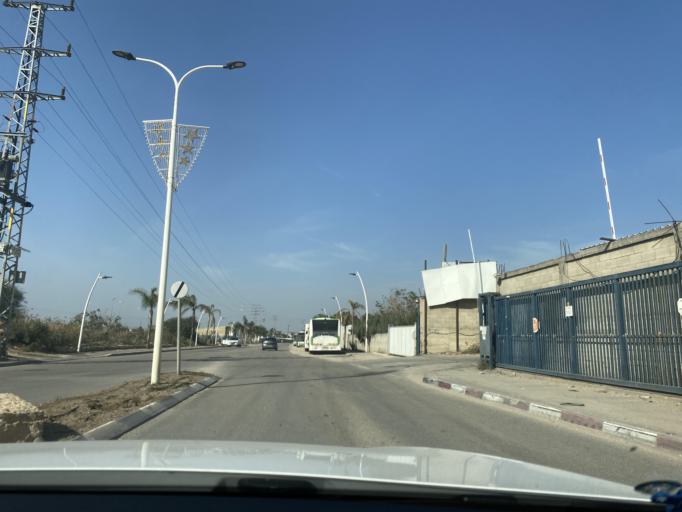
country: IL
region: Central District
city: Jaljulya
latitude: 32.1352
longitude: 34.9631
